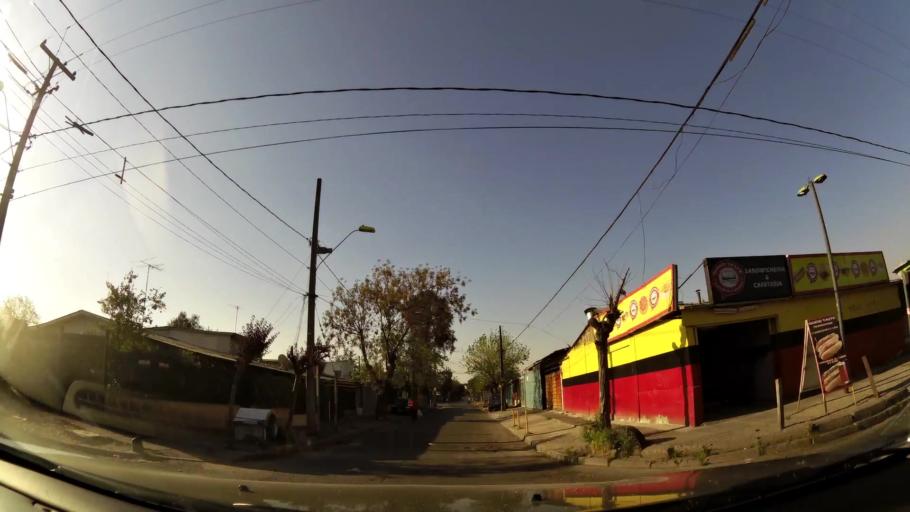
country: CL
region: Santiago Metropolitan
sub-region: Provincia de Santiago
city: La Pintana
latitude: -33.5827
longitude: -70.6603
